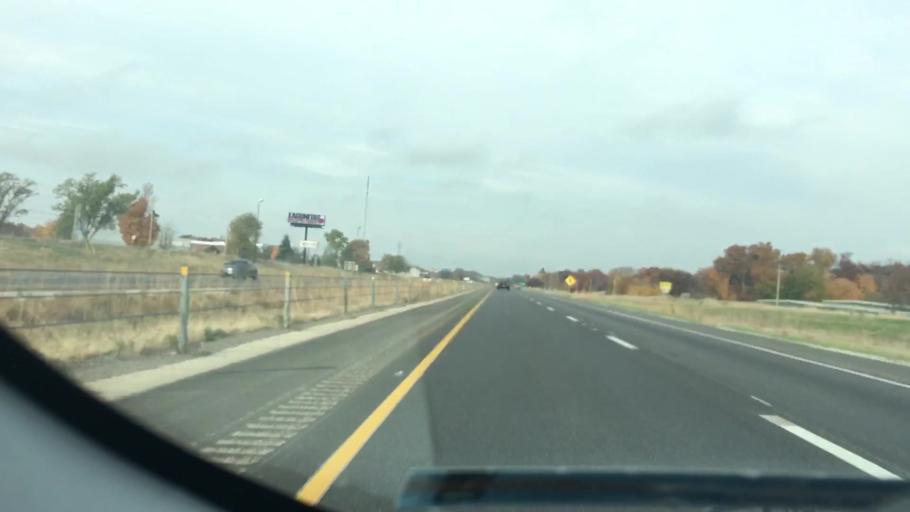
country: US
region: Illinois
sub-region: Tazewell County
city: East Peoria
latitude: 40.6440
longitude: -89.5421
